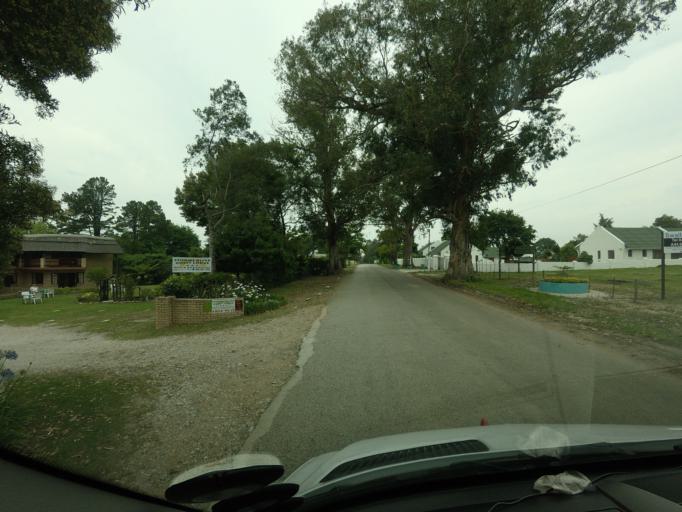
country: ZA
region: Eastern Cape
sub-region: Cacadu District Municipality
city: Kareedouw
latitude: -33.9710
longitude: 23.8874
